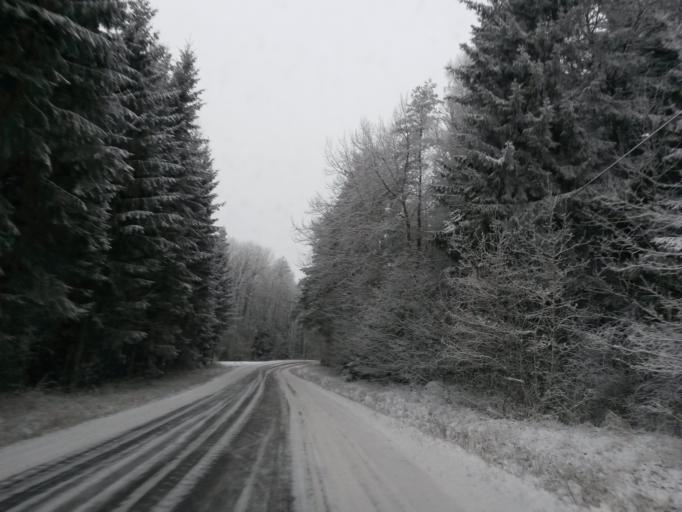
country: SE
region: Vaestra Goetaland
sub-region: Vara Kommun
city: Vara
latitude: 58.3532
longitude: 12.8743
